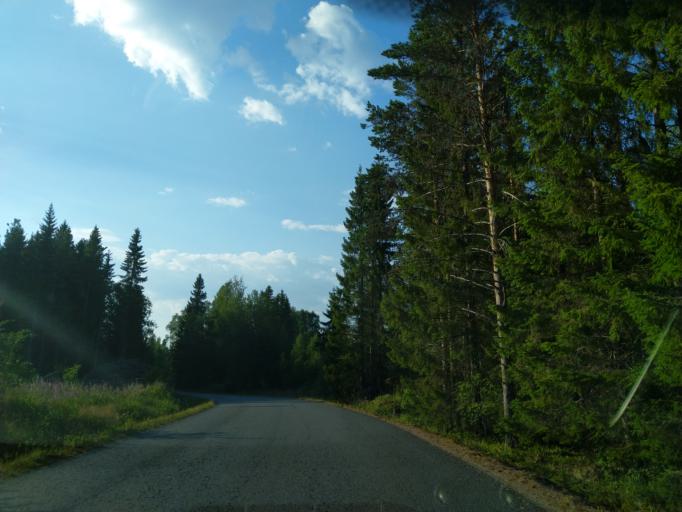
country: FI
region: Satakunta
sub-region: Pori
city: Laengelmaeki
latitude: 61.7881
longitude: 22.2099
